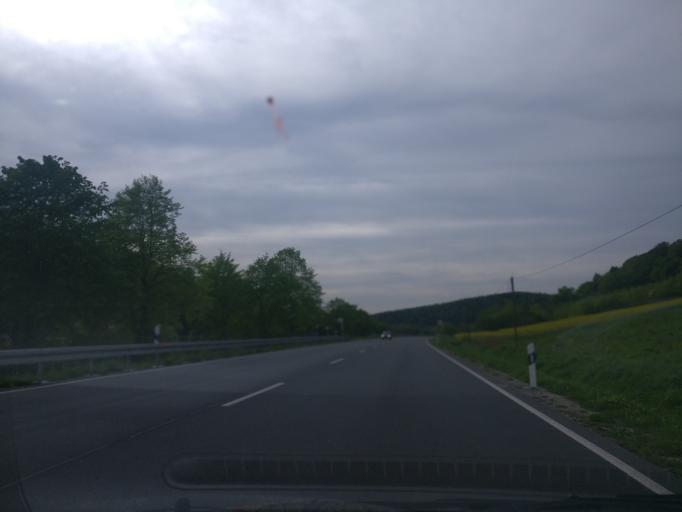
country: DE
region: Hesse
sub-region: Regierungsbezirk Kassel
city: Fuldatal
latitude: 51.3635
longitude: 9.5487
